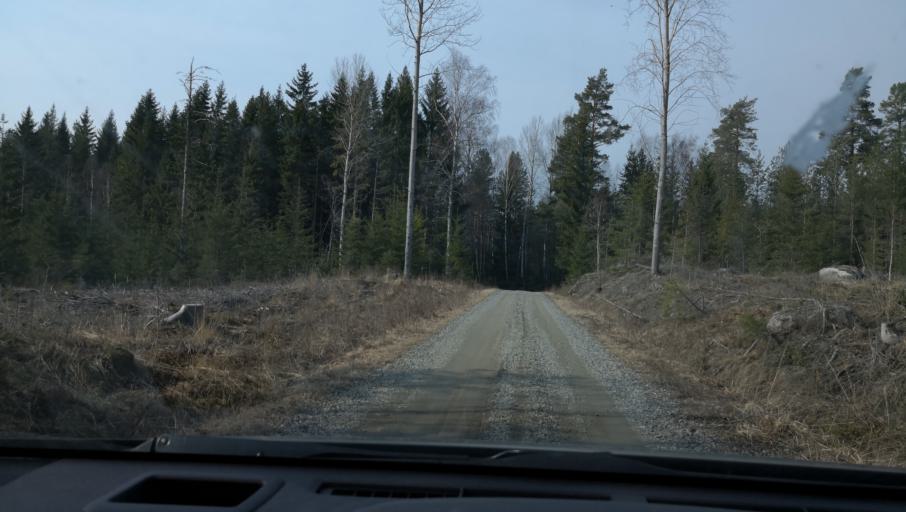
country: SE
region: OErebro
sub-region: Lindesbergs Kommun
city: Frovi
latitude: 59.3847
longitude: 15.4086
